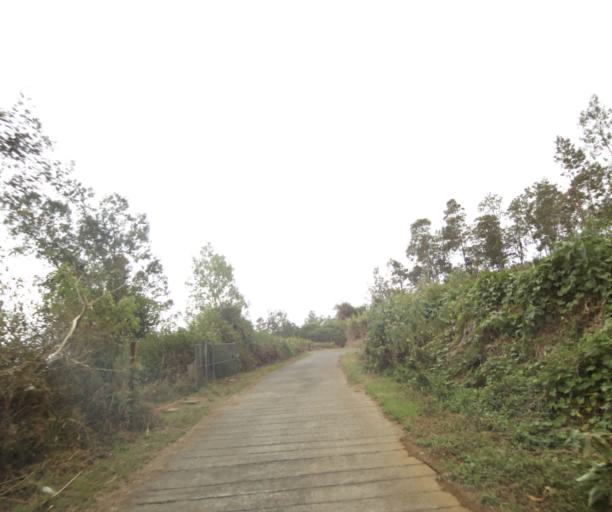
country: RE
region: Reunion
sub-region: Reunion
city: Saint-Paul
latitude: -21.0130
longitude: 55.3477
